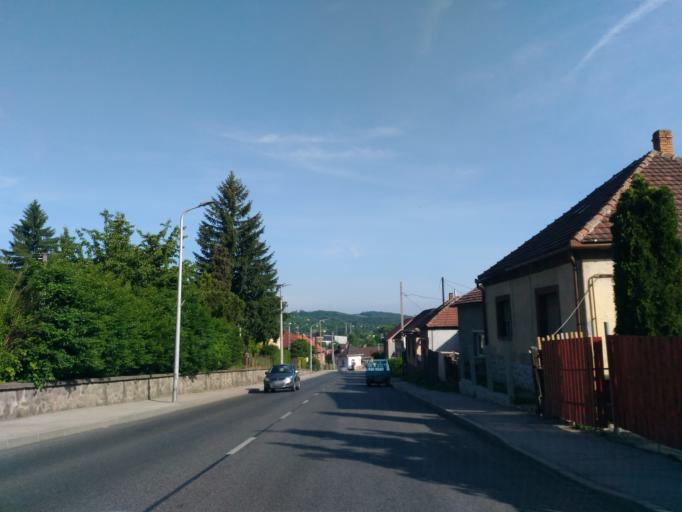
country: HU
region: Baranya
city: Komlo
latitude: 46.1881
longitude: 18.2603
